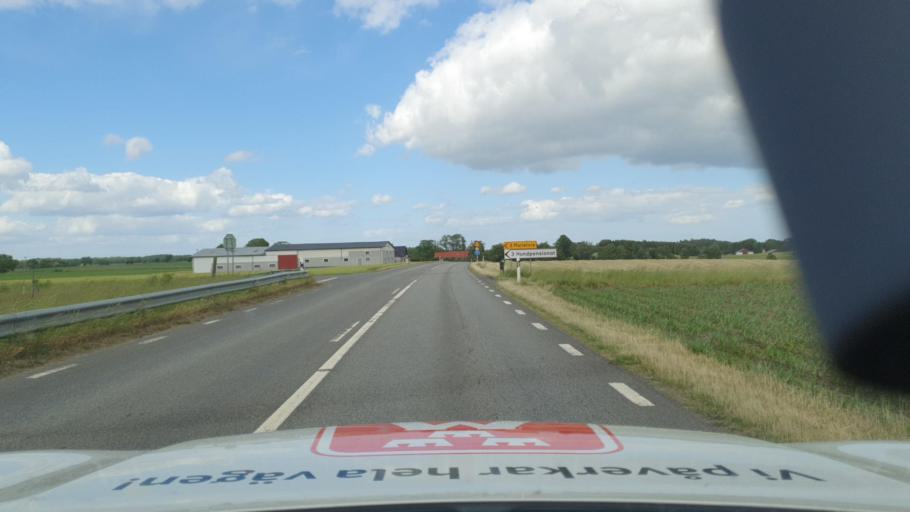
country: SE
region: Skane
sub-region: Tomelilla Kommun
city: Tomelilla
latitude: 55.5499
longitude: 14.0648
